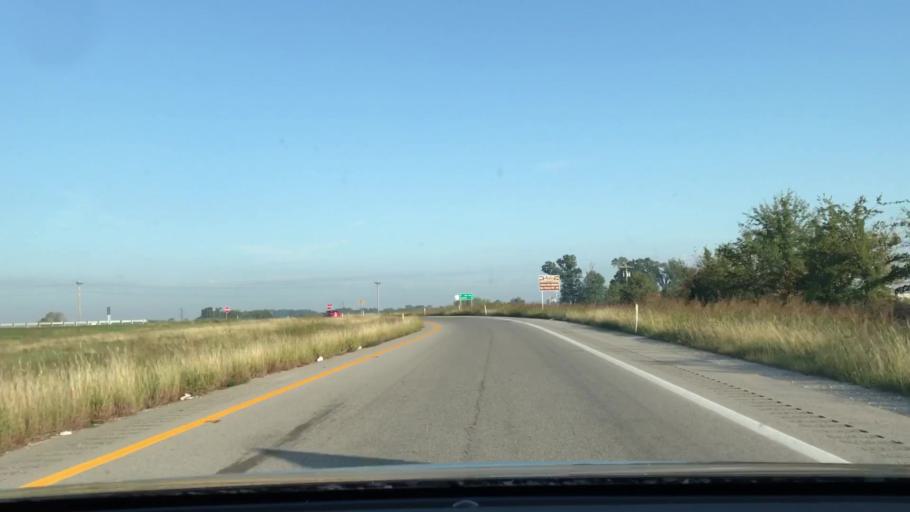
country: US
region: Kentucky
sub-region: Christian County
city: Oak Grove
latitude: 36.6823
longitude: -87.4026
